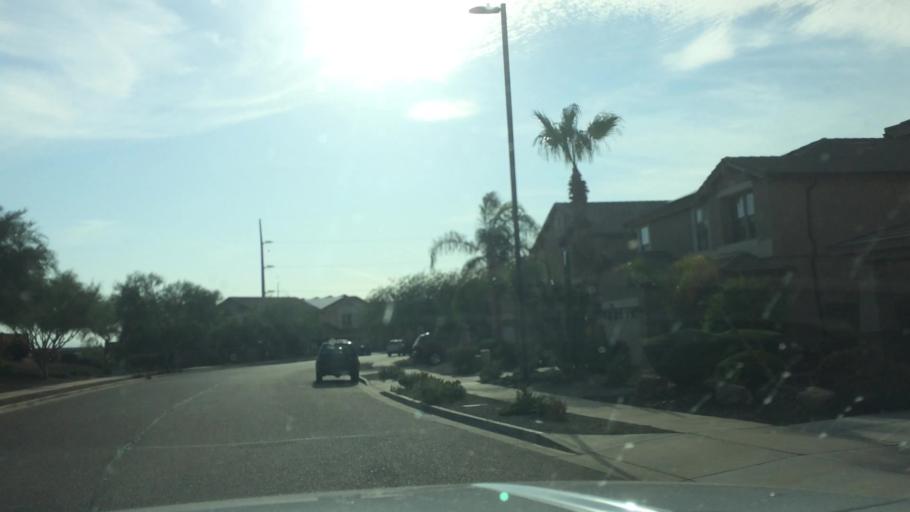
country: US
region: Arizona
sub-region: Maricopa County
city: Cave Creek
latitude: 33.6917
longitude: -112.0413
